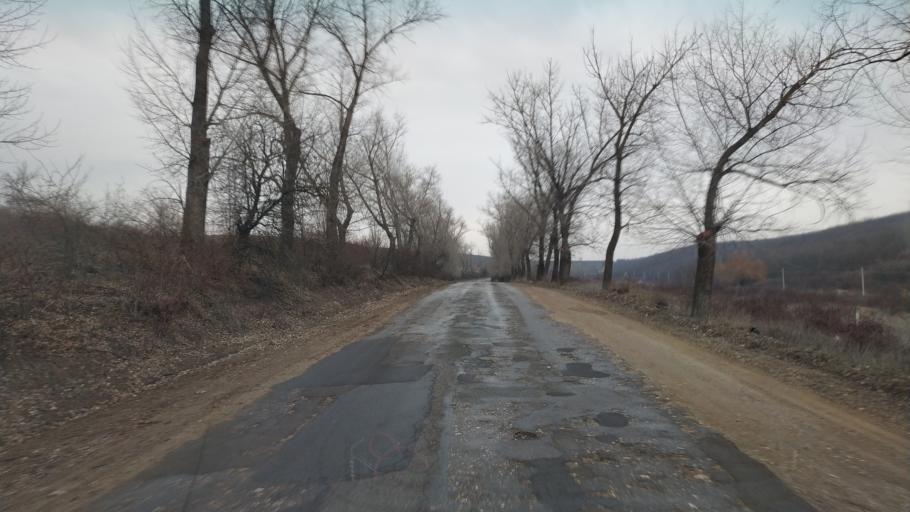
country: MD
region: Chisinau
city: Singera
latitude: 46.8441
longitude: 28.9837
